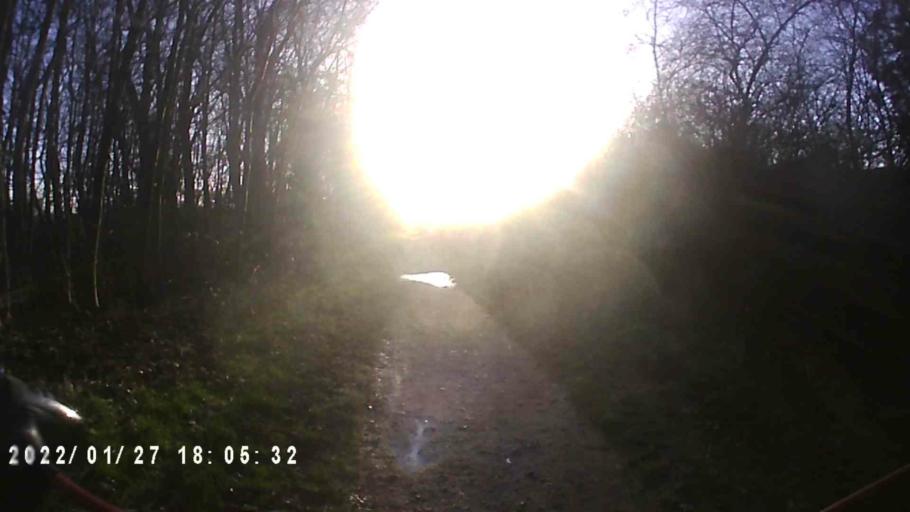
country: NL
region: Friesland
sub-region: Gemeente Dongeradeel
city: Anjum
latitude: 53.4058
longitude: 6.2172
